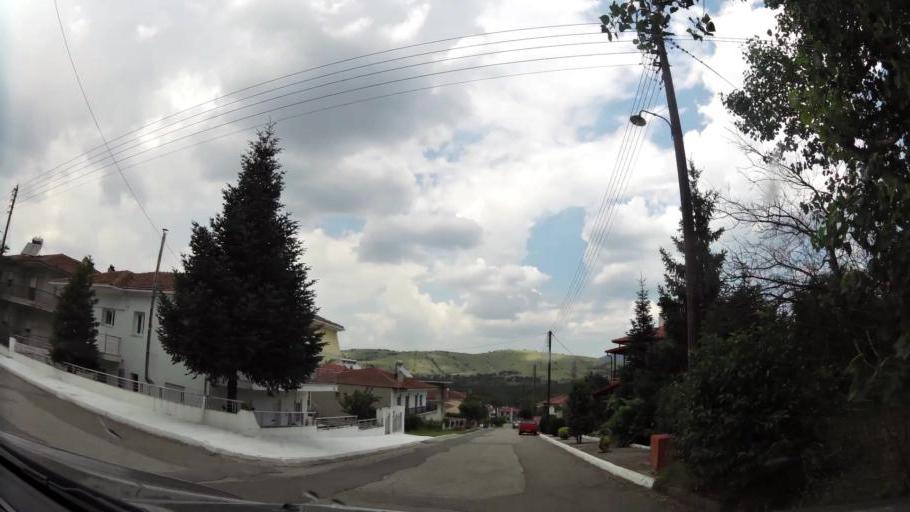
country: GR
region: West Macedonia
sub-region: Nomos Kozanis
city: Koila
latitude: 40.3253
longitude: 21.8238
